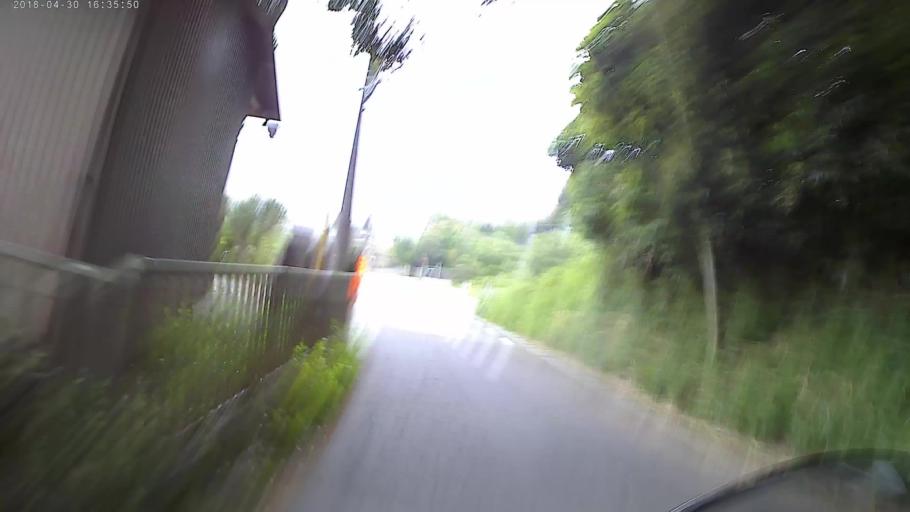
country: JP
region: Kanagawa
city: Atsugi
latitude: 35.4400
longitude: 139.4105
